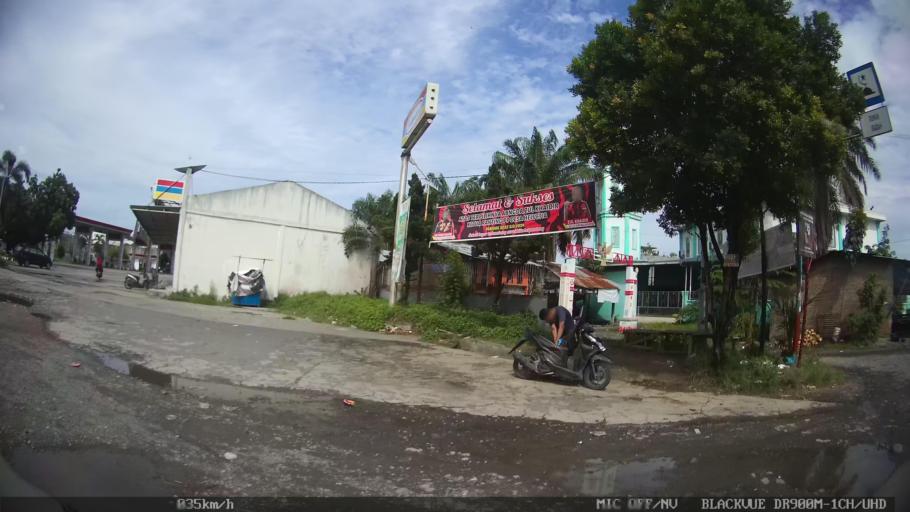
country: ID
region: North Sumatra
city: Medan
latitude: 3.6249
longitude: 98.6601
